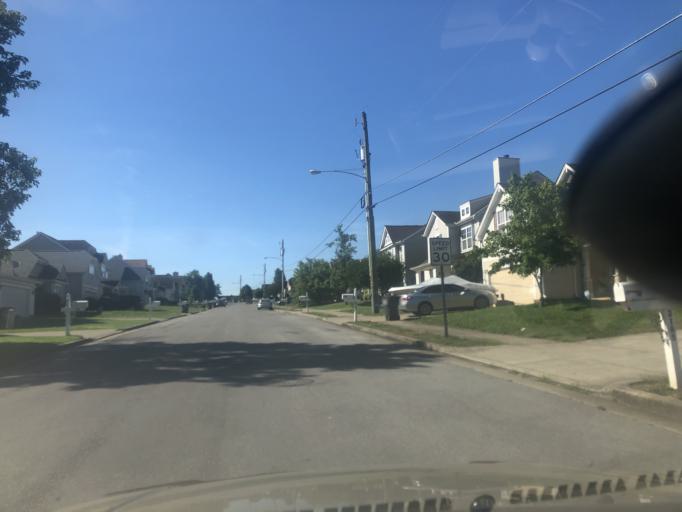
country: US
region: Tennessee
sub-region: Davidson County
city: Lakewood
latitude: 36.2462
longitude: -86.6669
